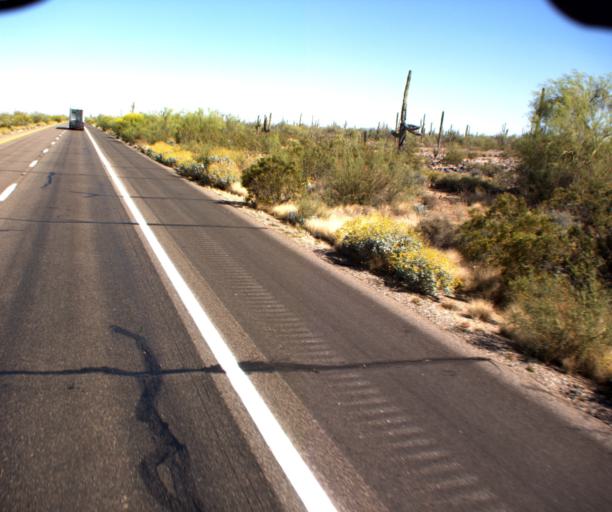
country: US
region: Arizona
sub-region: Pinal County
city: Maricopa
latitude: 32.8317
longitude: -112.0671
